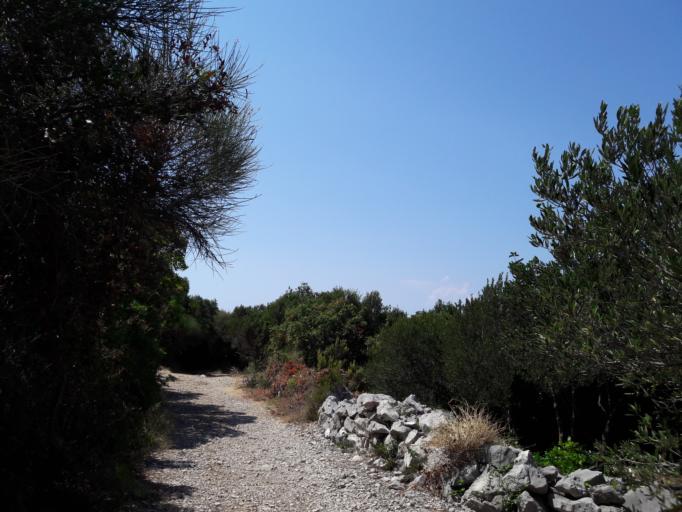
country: HR
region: Dubrovacko-Neretvanska
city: Orebic
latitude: 43.0227
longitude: 17.1633
